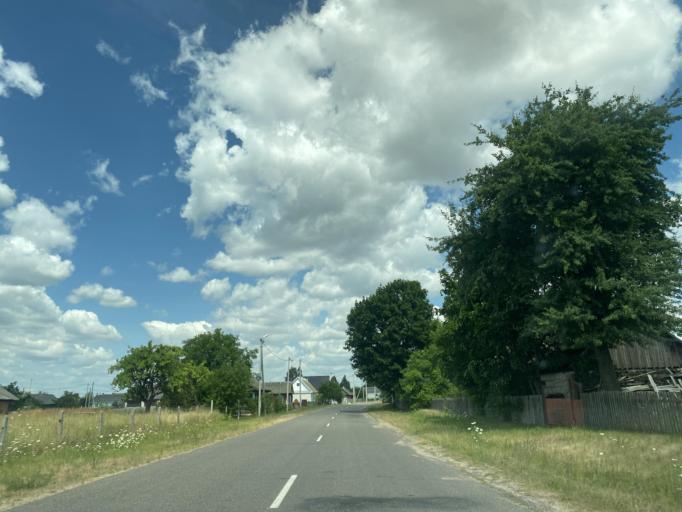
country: BY
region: Brest
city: Ivanava
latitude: 52.1685
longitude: 25.5592
